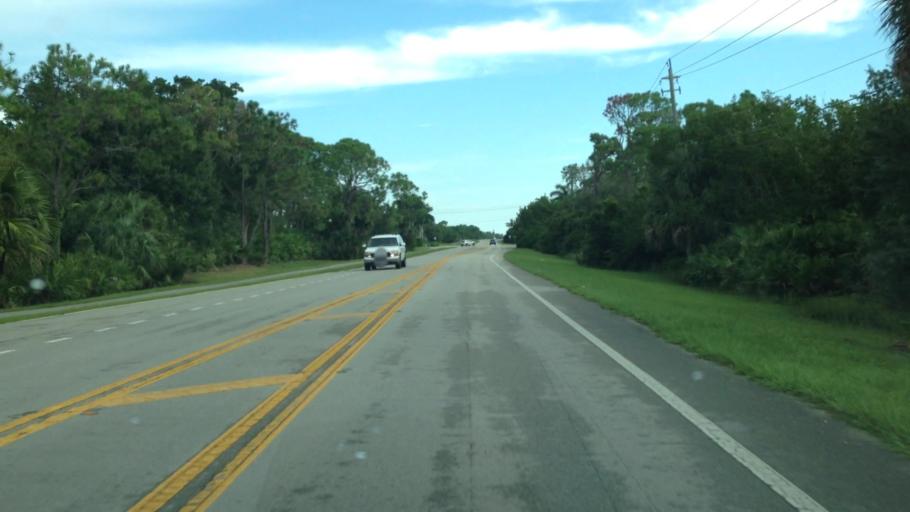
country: US
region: Florida
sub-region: Lee County
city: Bonita Springs
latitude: 26.3106
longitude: -81.8189
